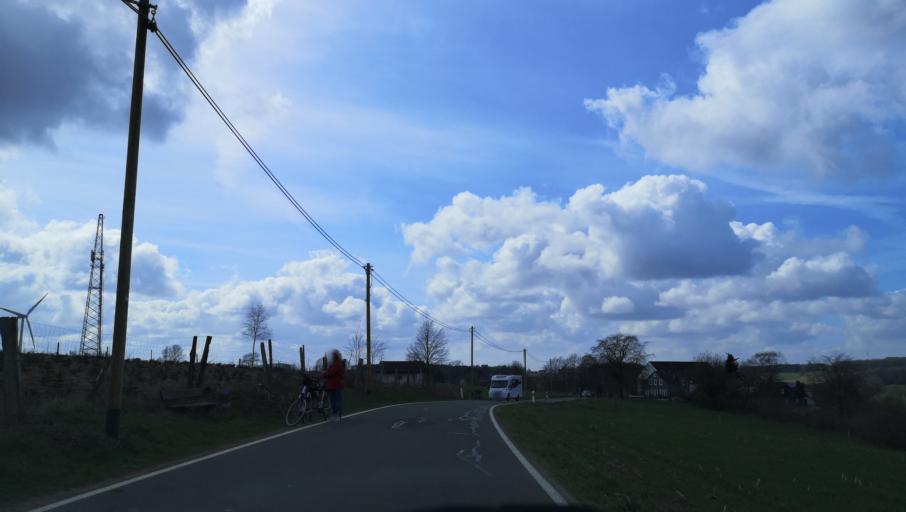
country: DE
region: North Rhine-Westphalia
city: Radevormwald
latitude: 51.2388
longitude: 7.3915
